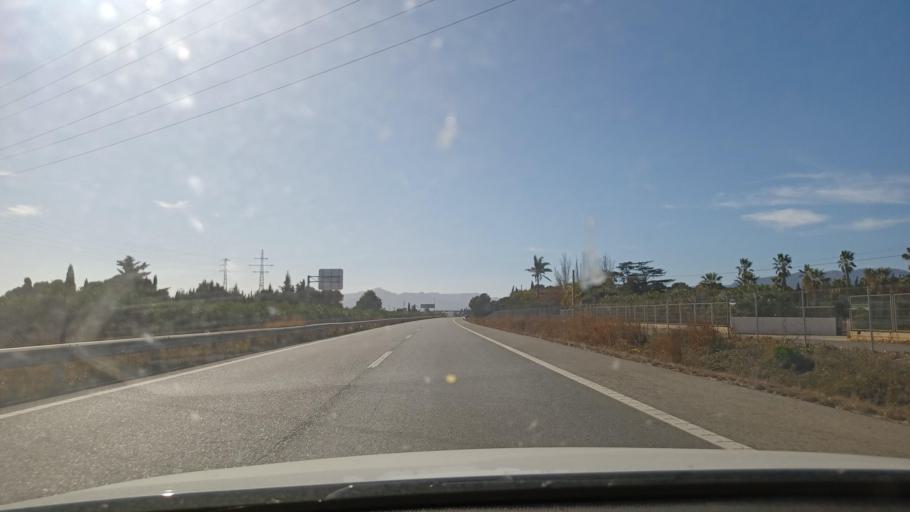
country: ES
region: Catalonia
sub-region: Provincia de Tarragona
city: Cambrils
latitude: 41.0781
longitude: 1.0305
